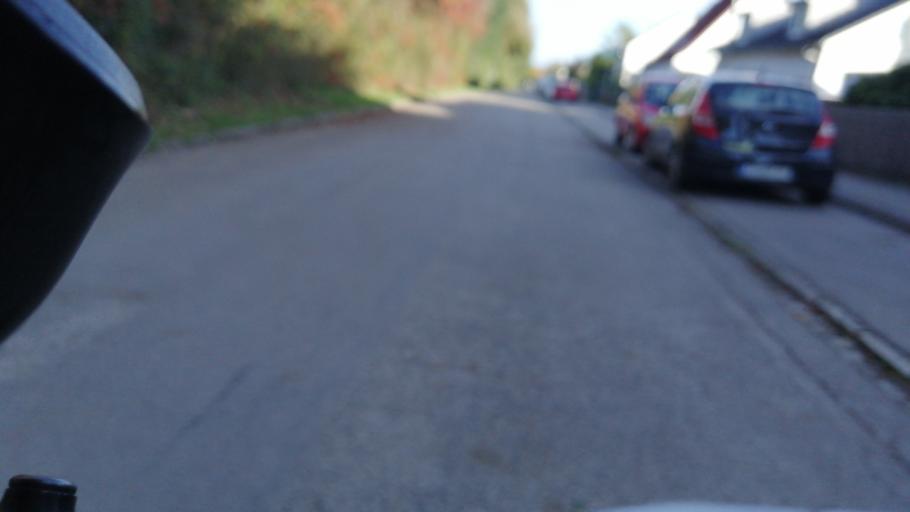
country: DE
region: Bavaria
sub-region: Upper Bavaria
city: Oberschleissheim
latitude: 48.2094
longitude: 11.5957
